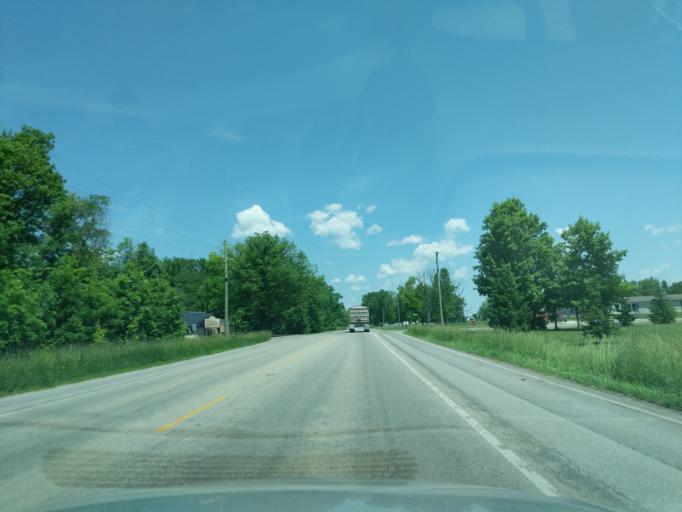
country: US
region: Indiana
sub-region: LaGrange County
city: Topeka
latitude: 41.5673
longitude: -85.5785
